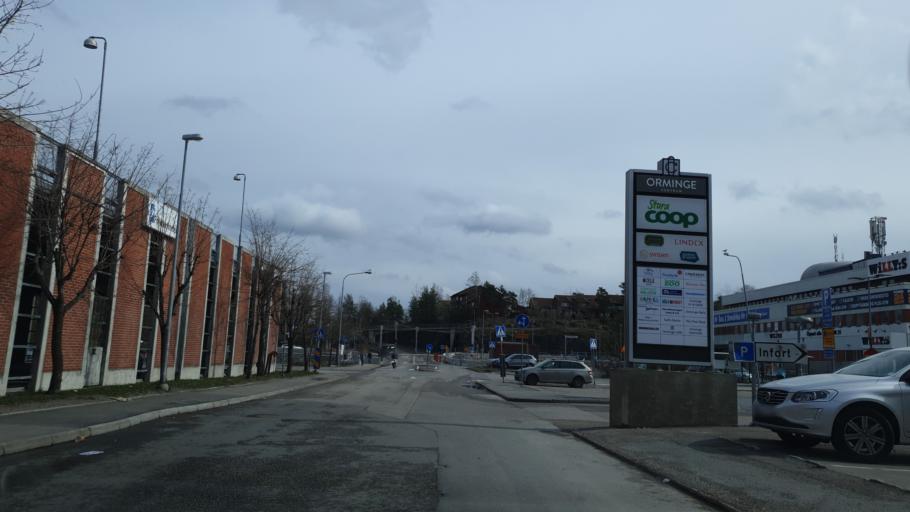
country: SE
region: Stockholm
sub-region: Nacka Kommun
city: Boo
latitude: 59.3270
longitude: 18.2581
